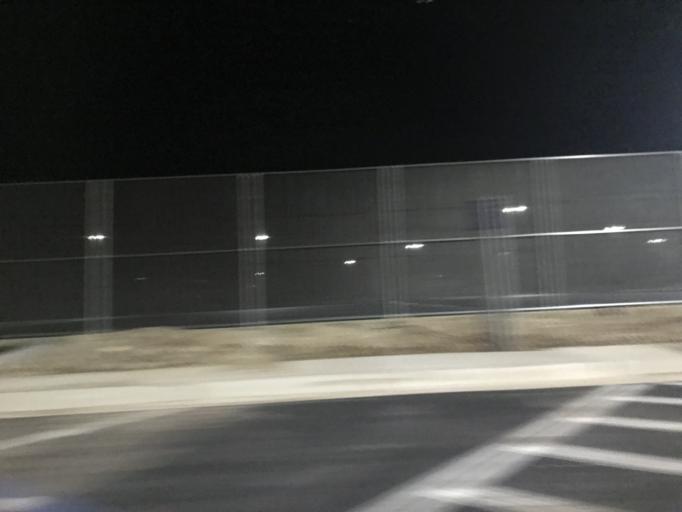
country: US
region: Texas
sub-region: Taylor County
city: Potosi
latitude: 32.3731
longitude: -99.7149
